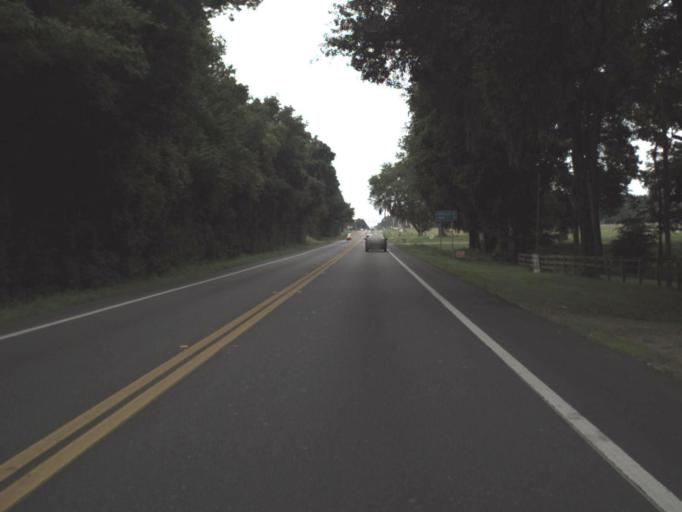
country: US
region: Florida
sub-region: Levy County
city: Williston
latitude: 29.3806
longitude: -82.4558
